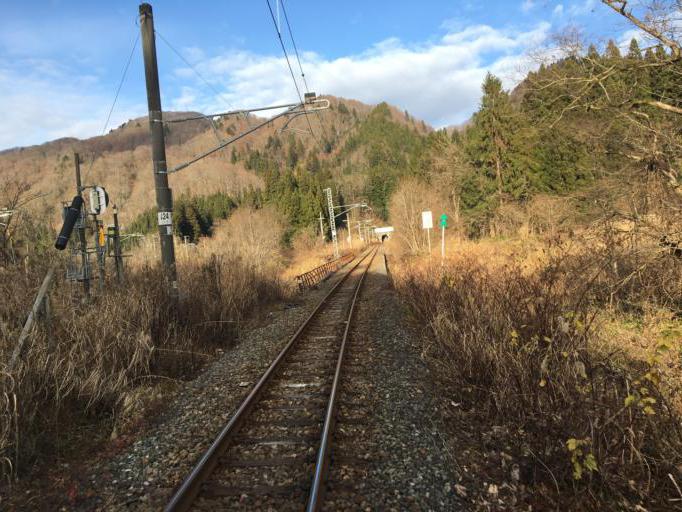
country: JP
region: Akita
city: Yuzawa
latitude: 38.9980
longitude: 140.3622
